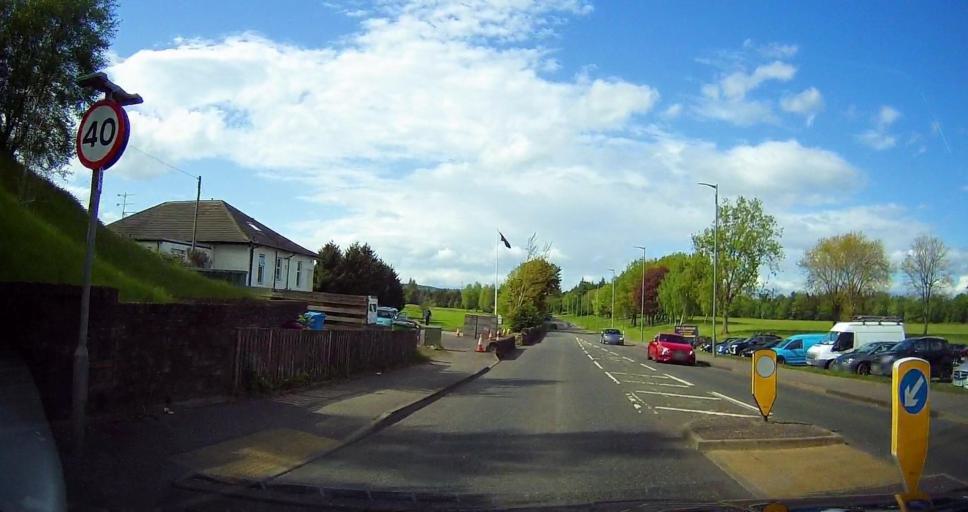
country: GB
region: Scotland
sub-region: Falkirk
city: Larbert
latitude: 56.0072
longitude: -3.8170
